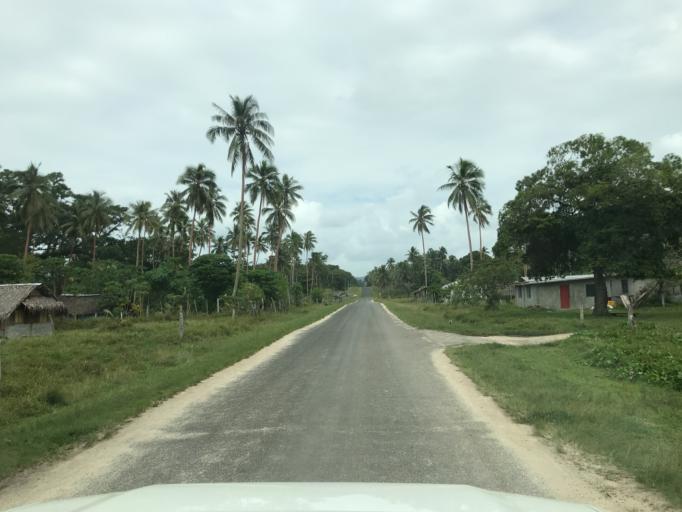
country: VU
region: Sanma
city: Port-Olry
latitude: -15.0444
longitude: 167.0720
